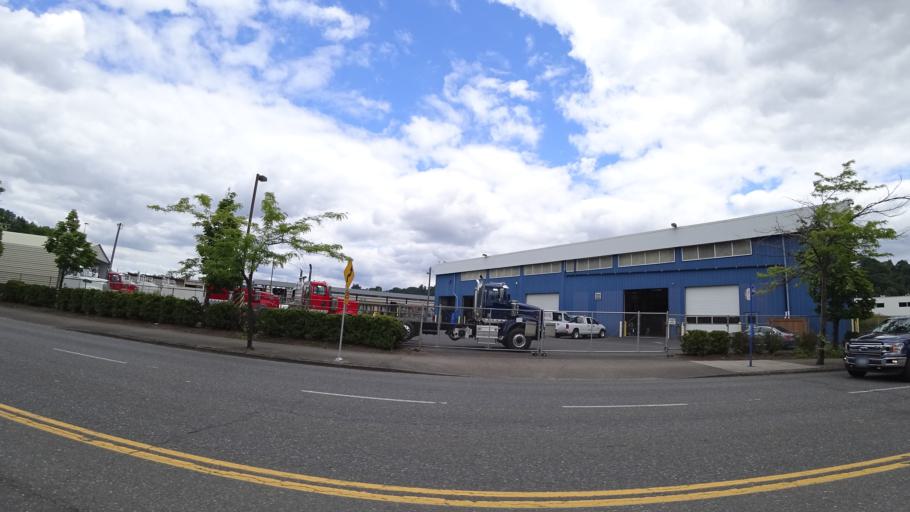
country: US
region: Oregon
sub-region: Multnomah County
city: Portland
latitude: 45.5624
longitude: -122.7048
